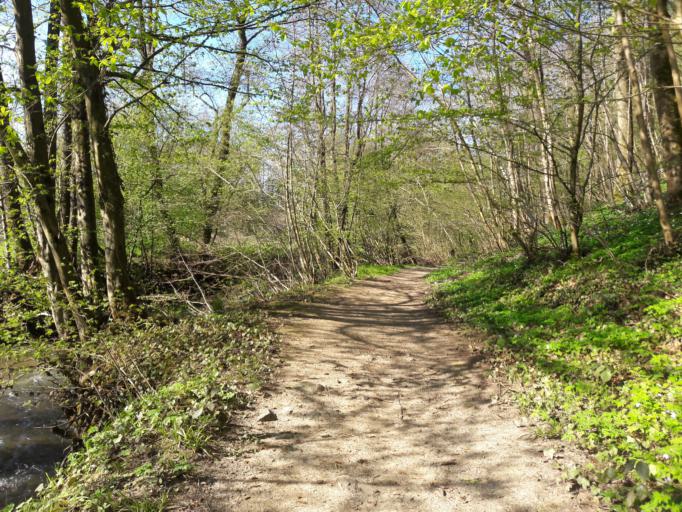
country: FR
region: Nord-Pas-de-Calais
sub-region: Departement du Nord
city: Ferriere-la-Grande
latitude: 50.2449
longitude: 4.0099
